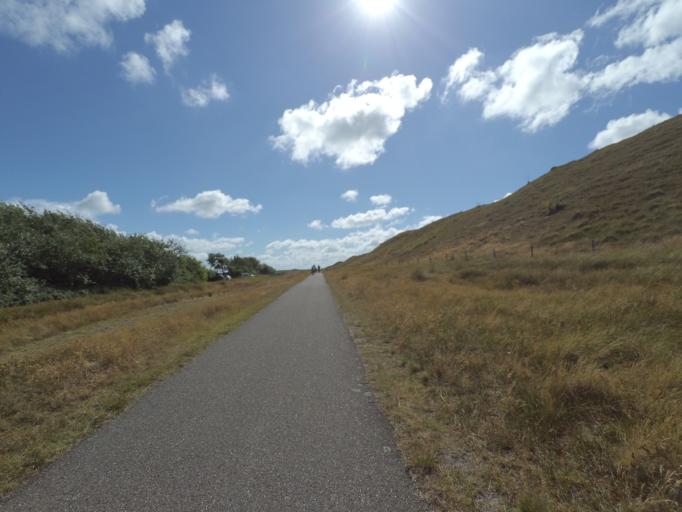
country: NL
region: North Holland
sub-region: Gemeente Texel
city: Den Burg
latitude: 53.1251
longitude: 4.8097
